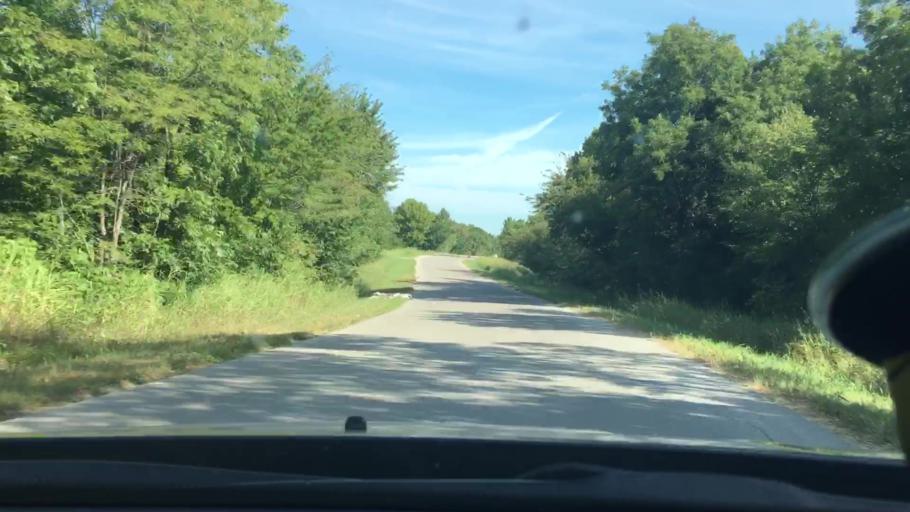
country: US
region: Oklahoma
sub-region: Carter County
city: Lone Grove
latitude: 34.2818
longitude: -97.2825
